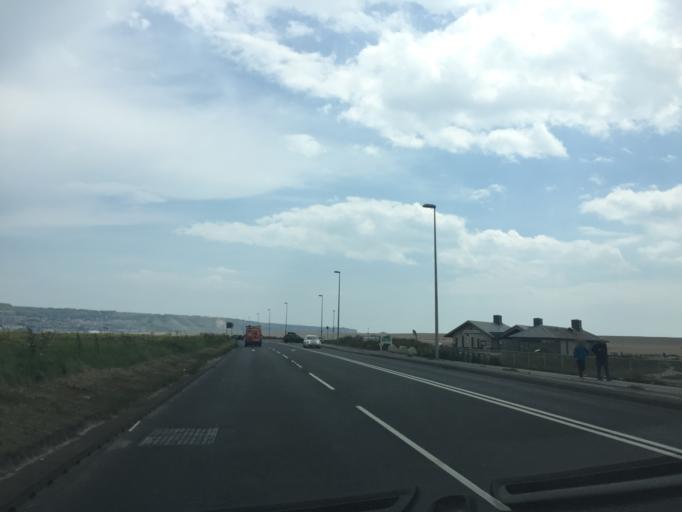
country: GB
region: England
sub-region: Dorset
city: Portland
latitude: 50.5800
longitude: -2.4697
